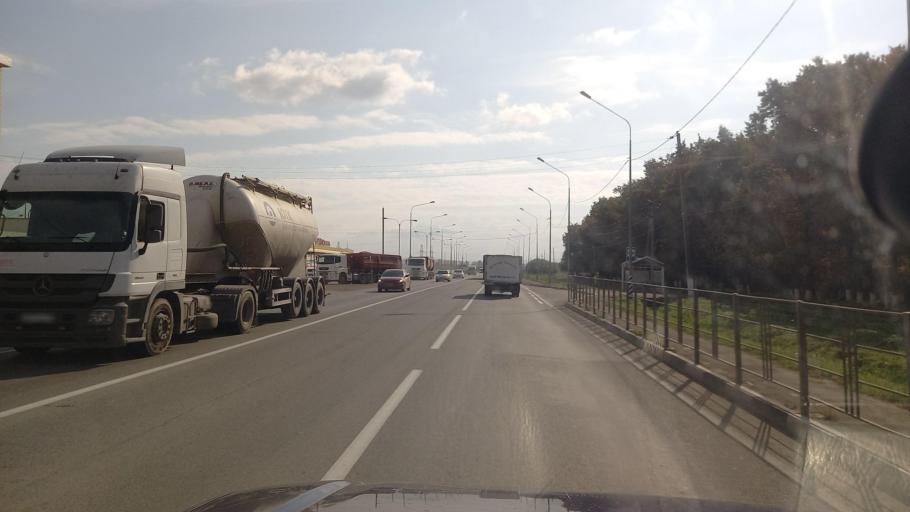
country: RU
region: Krasnodarskiy
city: Novoukrainskiy
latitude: 44.9088
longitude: 38.0224
